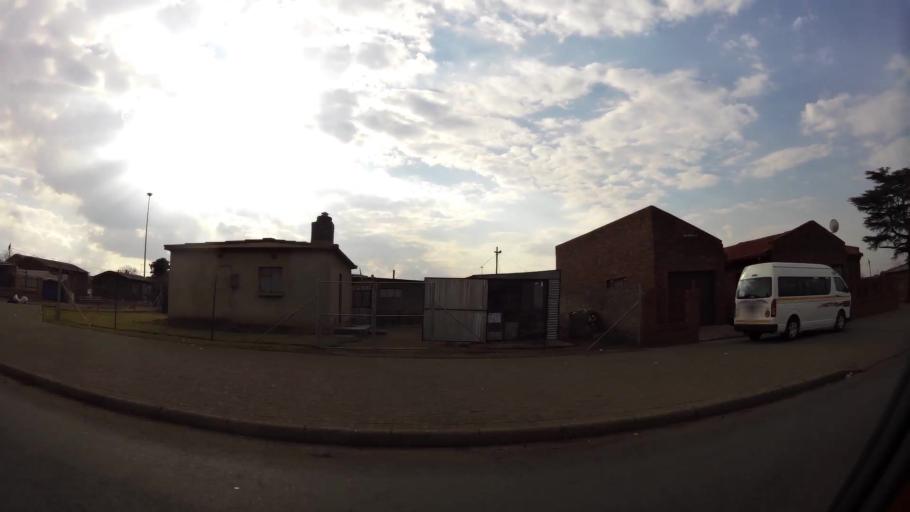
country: ZA
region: Gauteng
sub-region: Sedibeng District Municipality
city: Vereeniging
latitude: -26.6812
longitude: 27.8820
